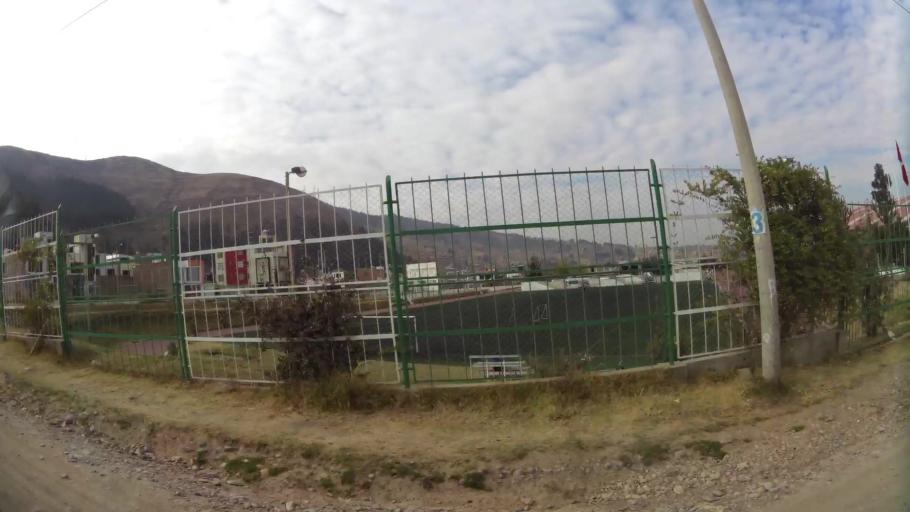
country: PE
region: Junin
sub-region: Provincia de Huancayo
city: Huancayo
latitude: -12.0445
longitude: -75.1891
